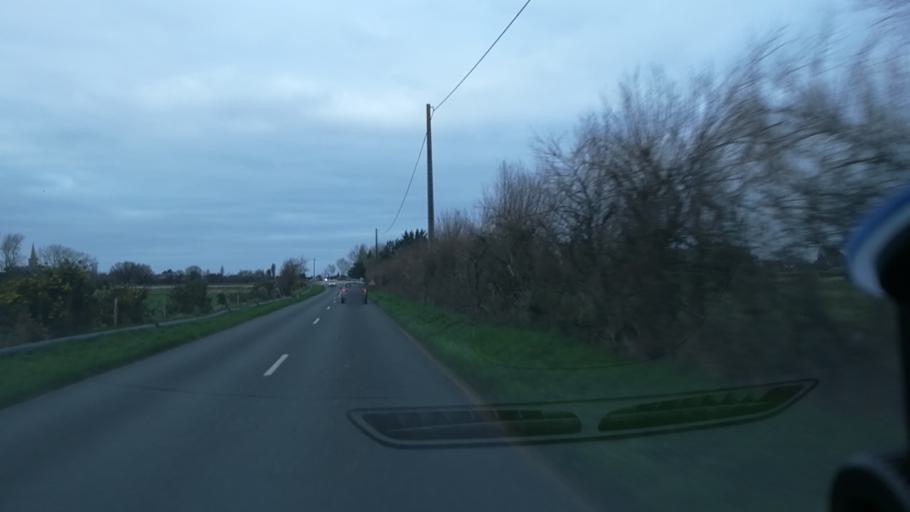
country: FR
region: Lower Normandy
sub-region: Departement de la Manche
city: Reville
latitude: 49.6100
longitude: -1.2569
